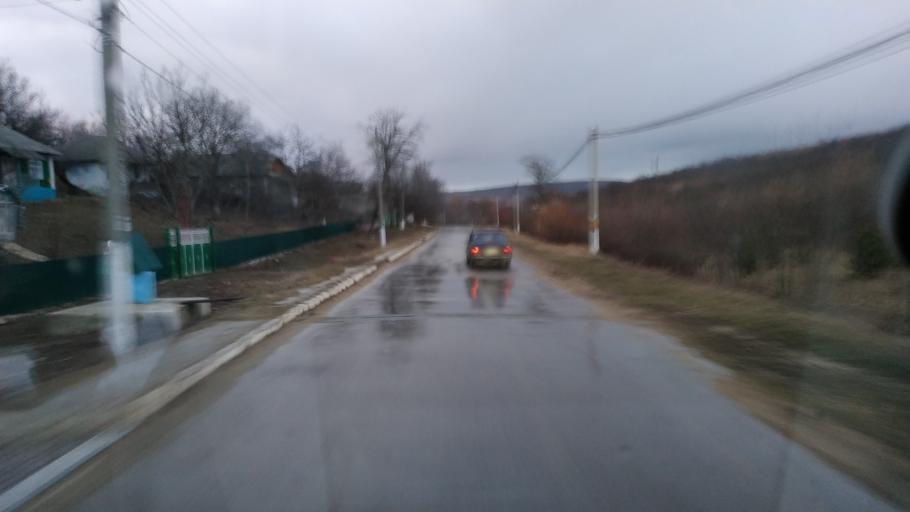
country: MD
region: Calarasi
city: Calarasi
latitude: 47.3776
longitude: 28.3226
